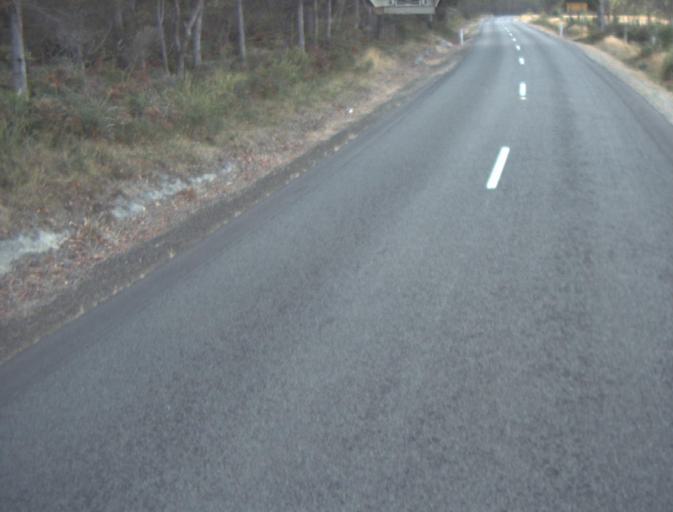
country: AU
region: Tasmania
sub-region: Dorset
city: Bridport
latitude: -41.1498
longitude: 147.2347
